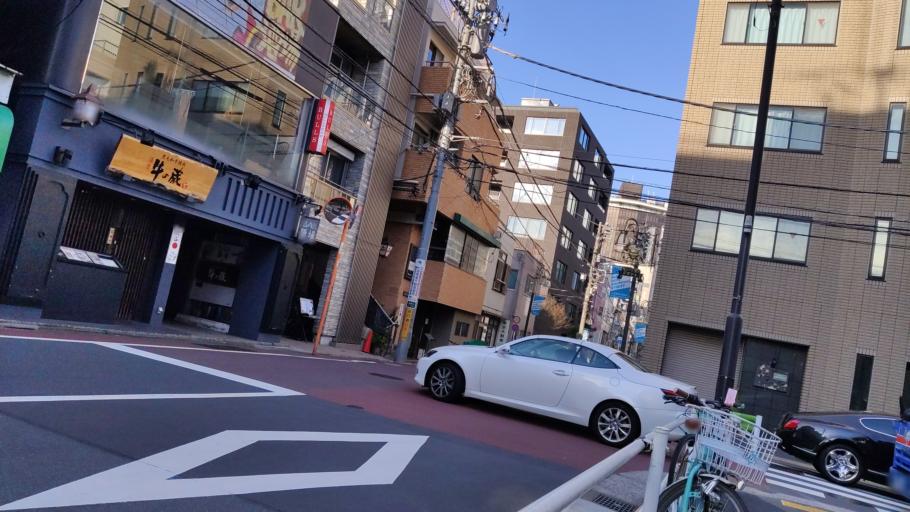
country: JP
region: Tokyo
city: Tokyo
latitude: 35.6570
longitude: 139.7182
